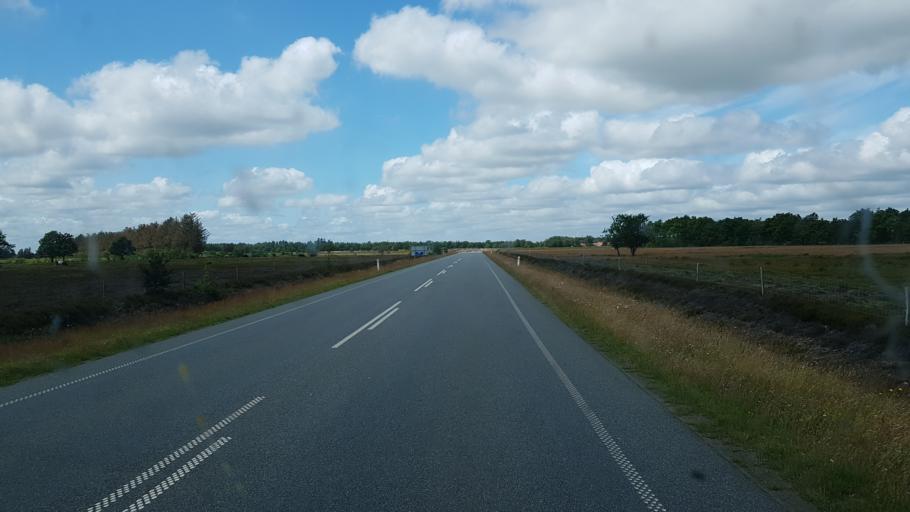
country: DK
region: South Denmark
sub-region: Billund Kommune
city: Grindsted
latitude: 55.7427
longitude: 8.9145
